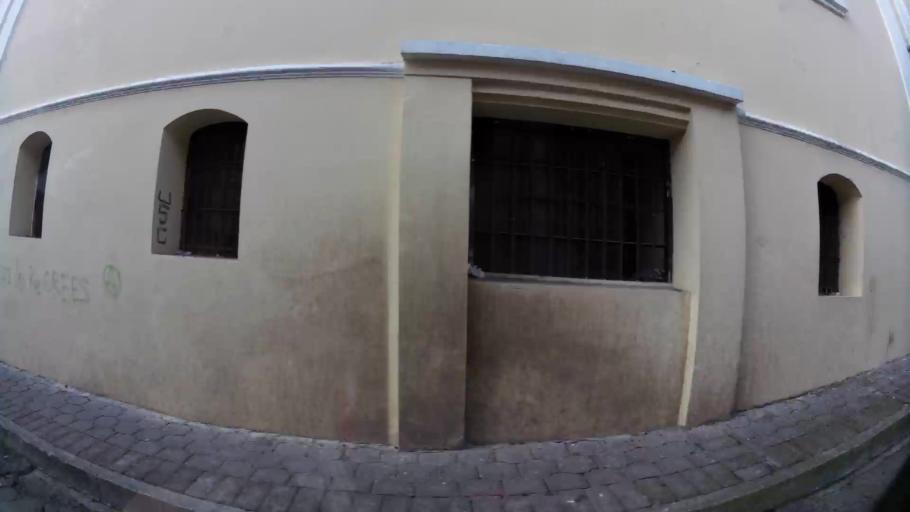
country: EC
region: Pichincha
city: Quito
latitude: -0.2234
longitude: -78.5048
